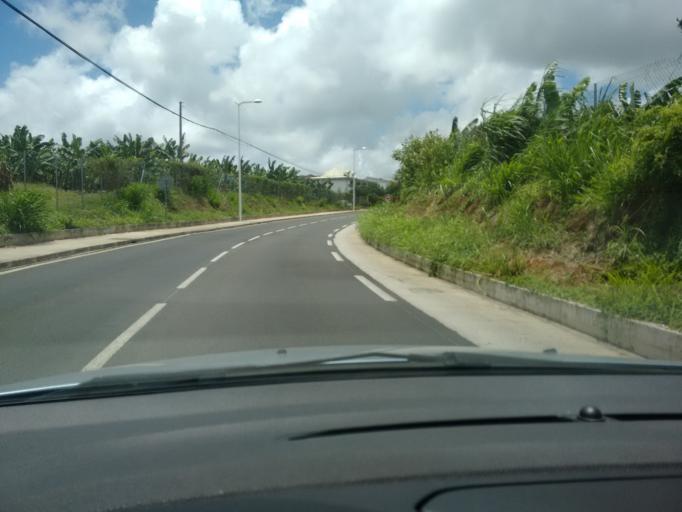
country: MQ
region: Martinique
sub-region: Martinique
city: Saint-Joseph
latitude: 14.6740
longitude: -61.0253
